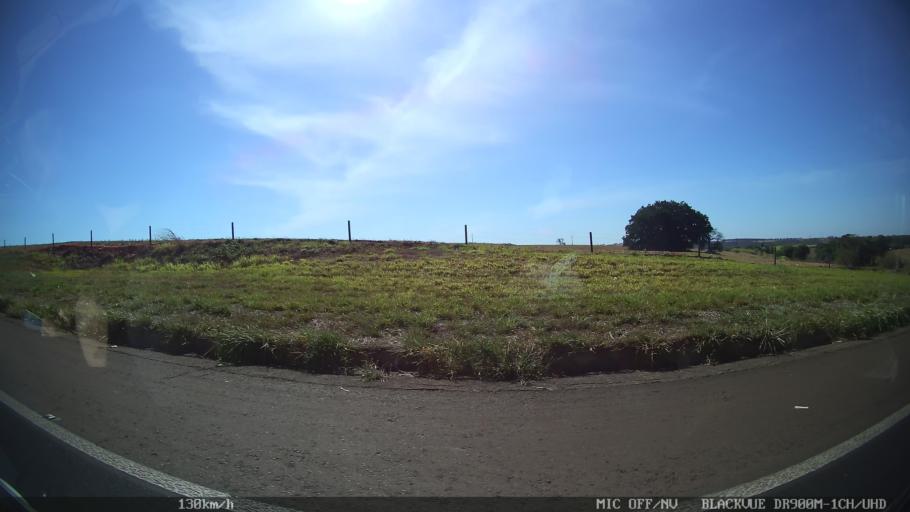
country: BR
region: Sao Paulo
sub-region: Olimpia
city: Olimpia
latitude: -20.6236
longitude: -48.7764
